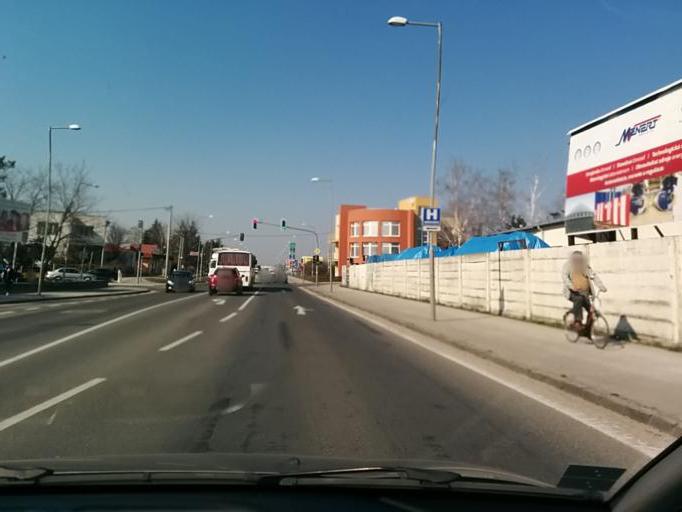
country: SK
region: Trnavsky
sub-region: Okres Galanta
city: Galanta
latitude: 48.1965
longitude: 17.7338
